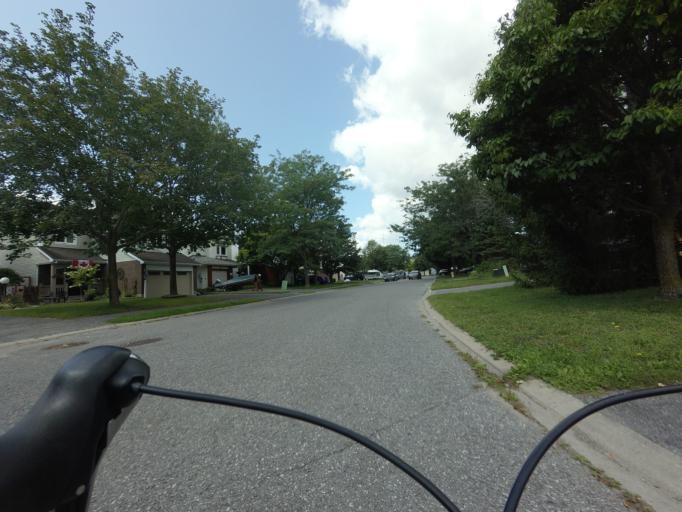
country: CA
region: Ontario
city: Bells Corners
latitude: 45.2838
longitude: -75.8582
